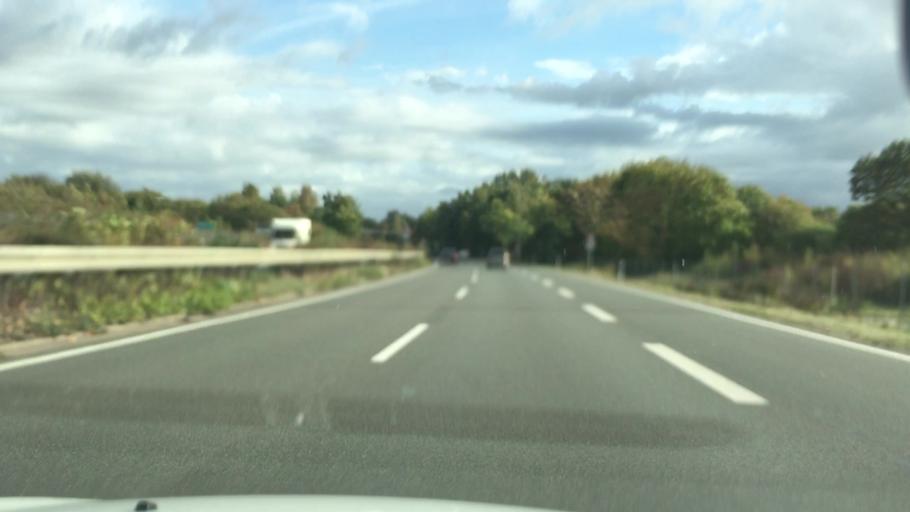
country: DE
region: Lower Saxony
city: Garbsen
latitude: 52.4593
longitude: 9.5407
